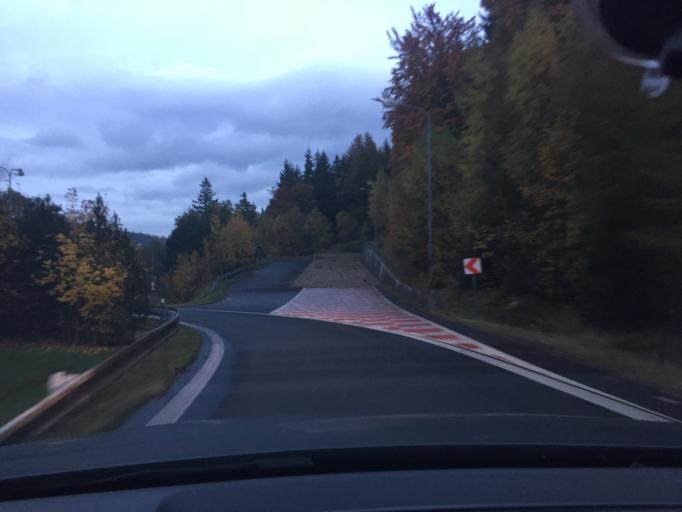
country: CZ
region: Ustecky
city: Dubi
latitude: 50.6895
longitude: 13.7765
